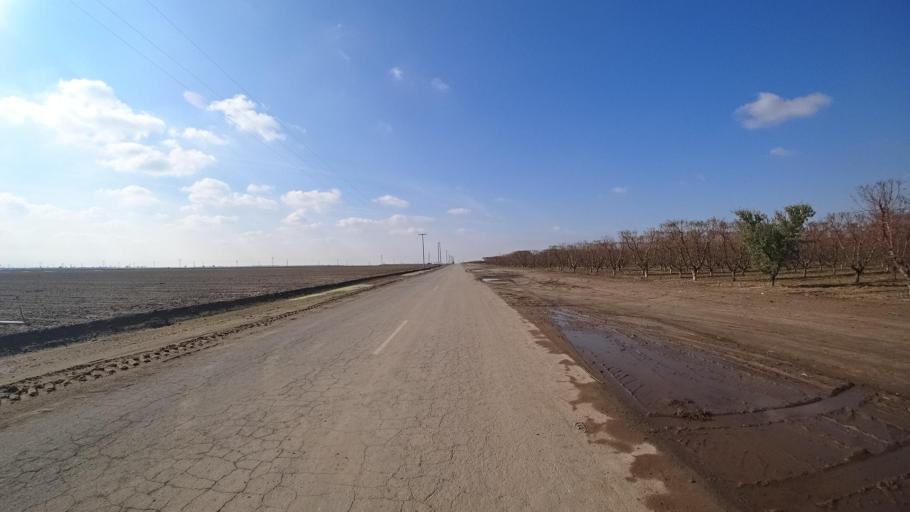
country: US
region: California
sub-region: Kern County
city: Arvin
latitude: 35.2530
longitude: -118.7998
